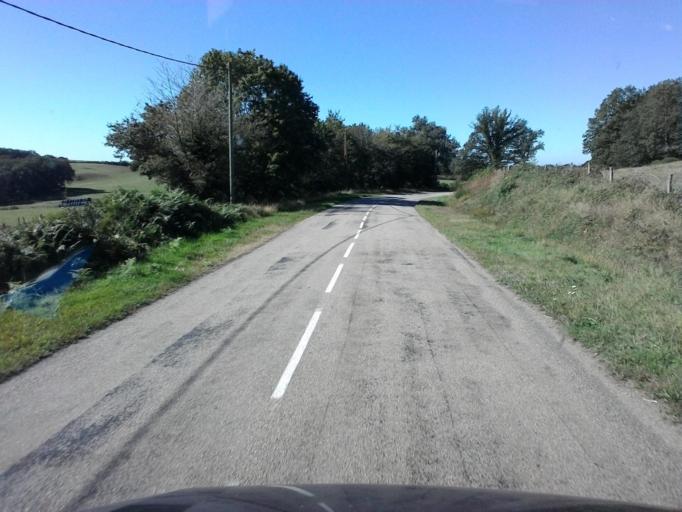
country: FR
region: Bourgogne
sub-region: Departement de la Nievre
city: Lormes
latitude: 47.2747
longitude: 3.8372
